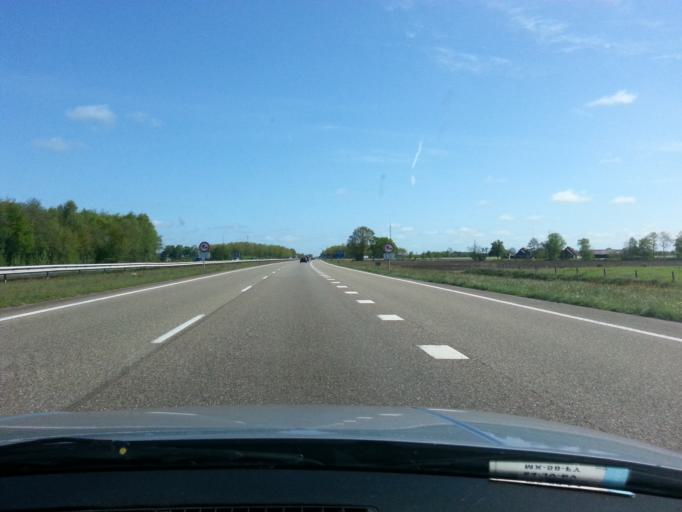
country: NL
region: Friesland
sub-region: Gemeente Opsterland
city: Tijnje
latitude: 53.0244
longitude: 6.0124
